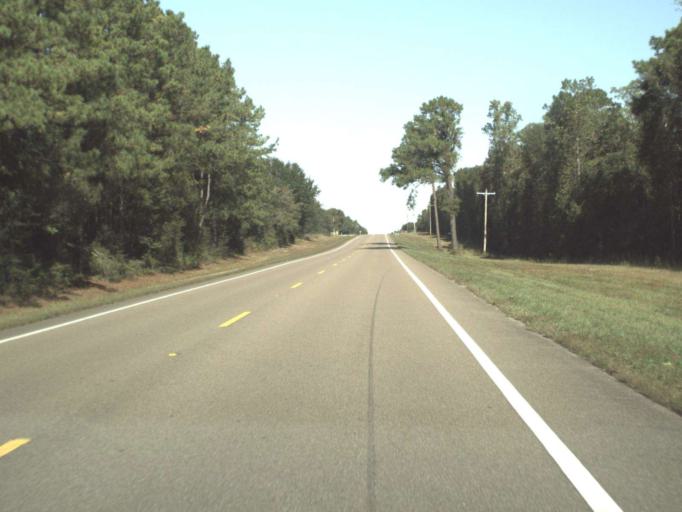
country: US
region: Florida
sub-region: Walton County
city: Freeport
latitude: 30.5589
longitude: -85.9183
